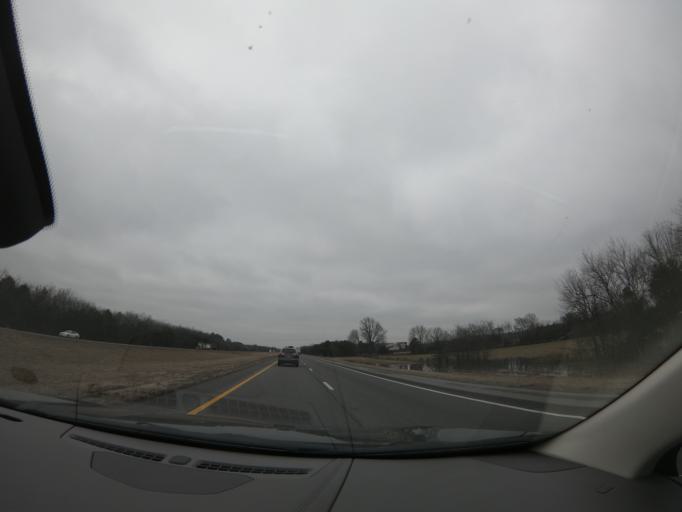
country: US
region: Tennessee
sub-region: Rutherford County
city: Plainview
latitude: 35.6833
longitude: -86.2901
